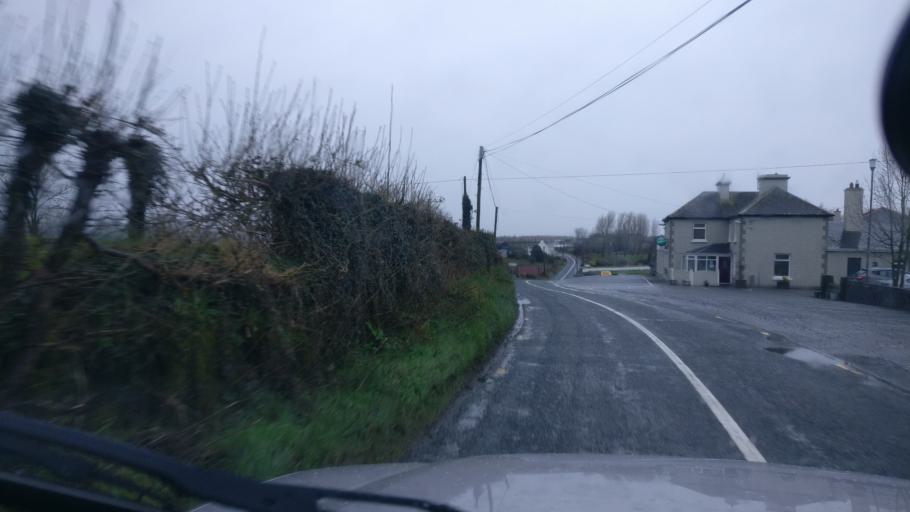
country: IE
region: Connaught
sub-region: County Galway
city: Loughrea
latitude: 53.1144
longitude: -8.4400
